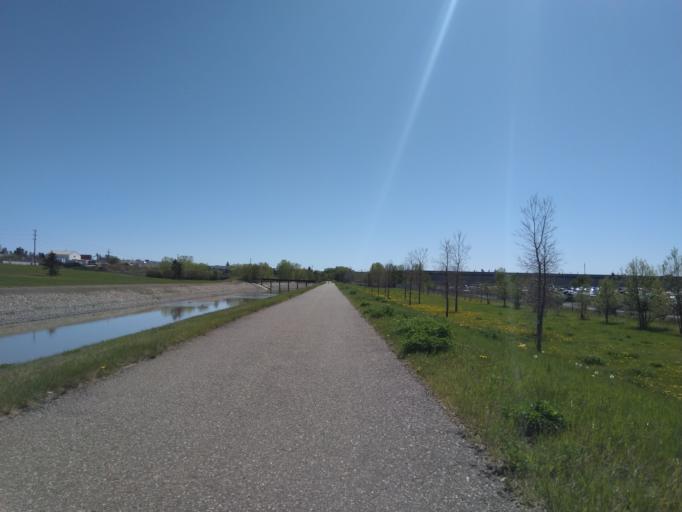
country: CA
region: Alberta
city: Calgary
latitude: 51.0020
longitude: -114.0051
